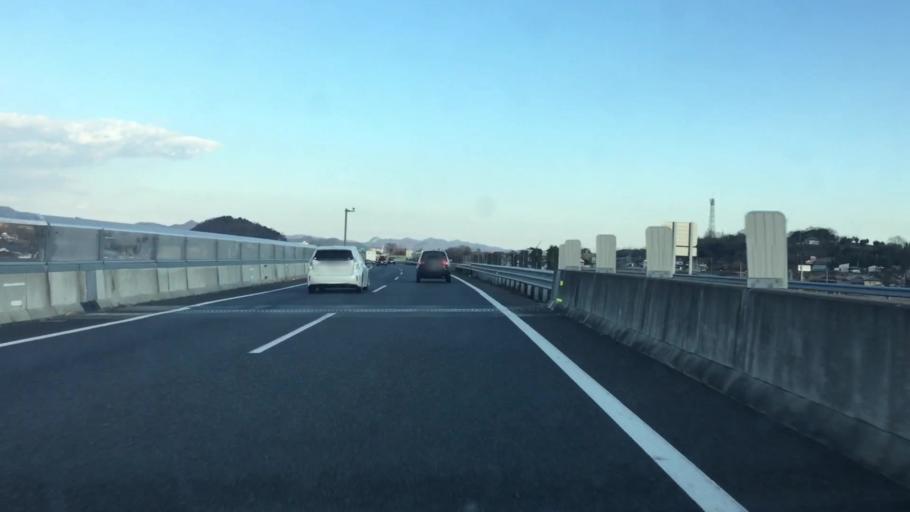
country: JP
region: Gunma
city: Ota
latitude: 36.3361
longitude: 139.3576
